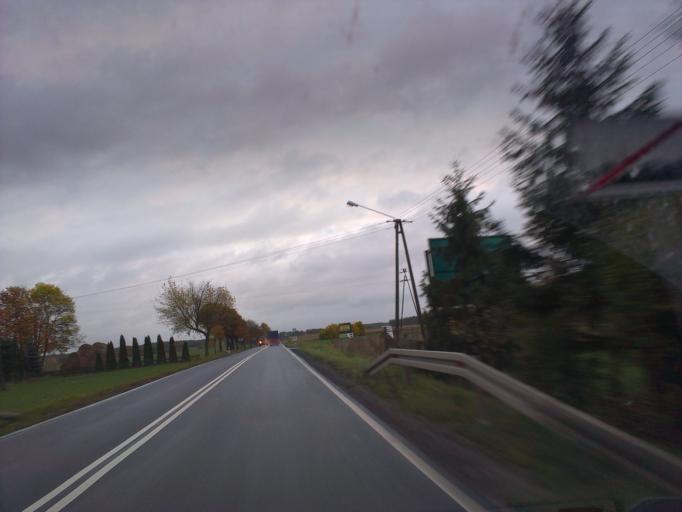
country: PL
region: Kujawsko-Pomorskie
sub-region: Powiat tucholski
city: Lubiewo
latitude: 53.5041
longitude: 18.0105
